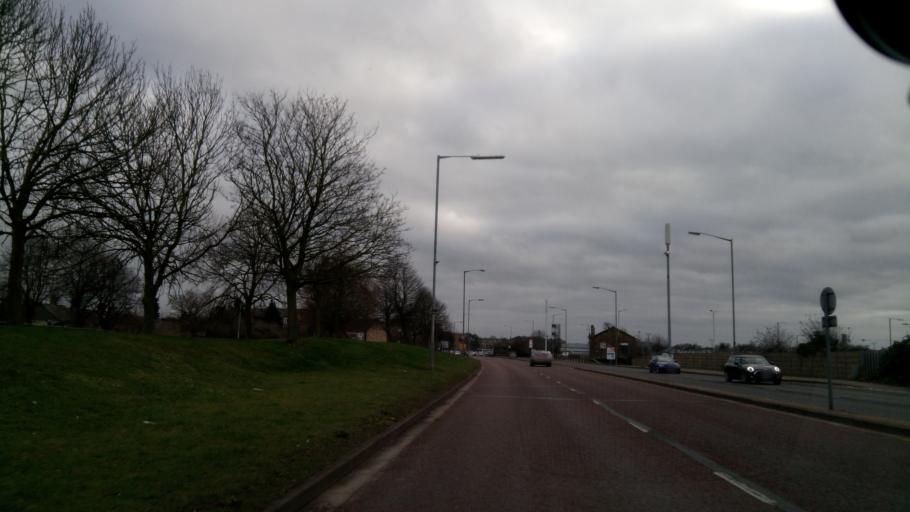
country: GB
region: England
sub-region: Peterborough
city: Peterborough
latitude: 52.5795
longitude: -0.2510
